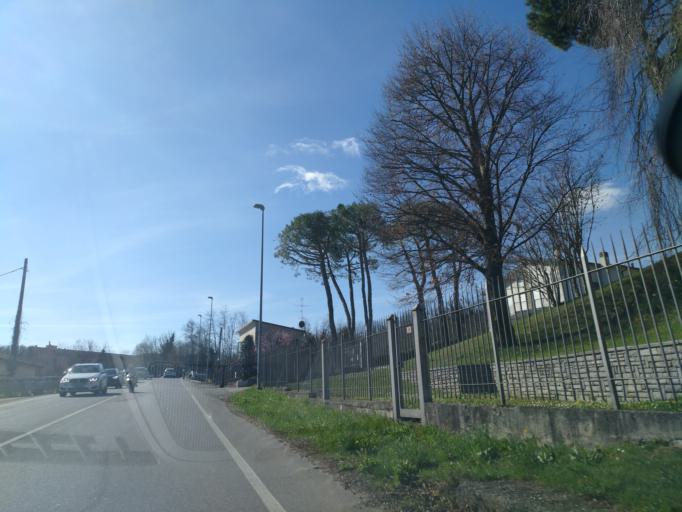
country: IT
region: Lombardy
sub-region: Provincia di Como
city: Anzano del Parco
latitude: 45.7660
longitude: 9.2000
